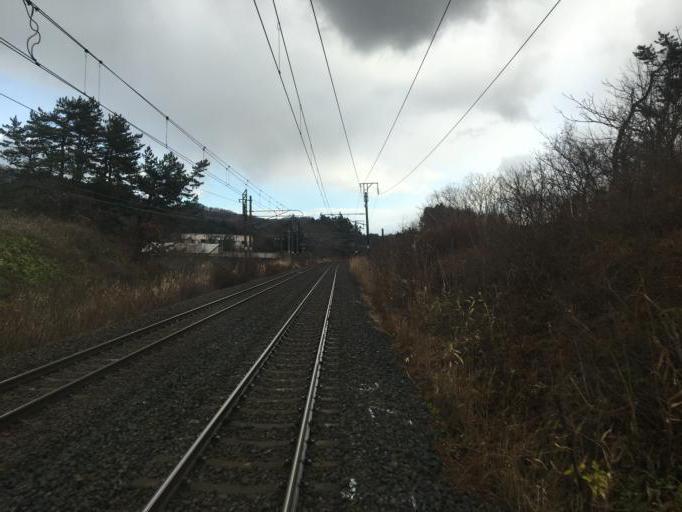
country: JP
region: Aomori
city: Aomori Shi
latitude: 40.9176
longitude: 140.8812
